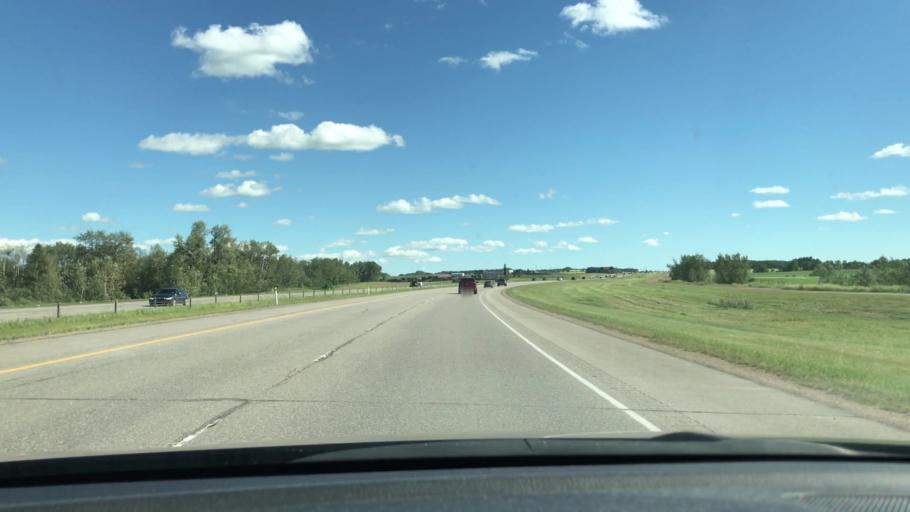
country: CA
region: Alberta
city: Penhold
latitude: 52.1810
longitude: -113.8149
